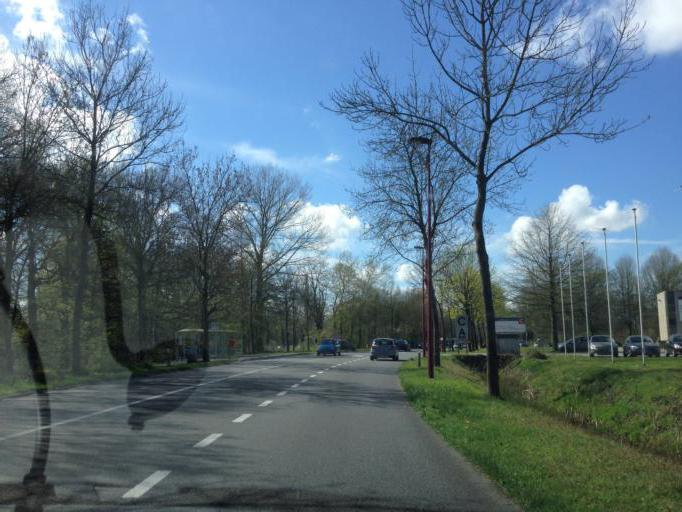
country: BE
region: Flanders
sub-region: Provincie Limburg
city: Diepenbeek
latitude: 50.9296
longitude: 5.3938
